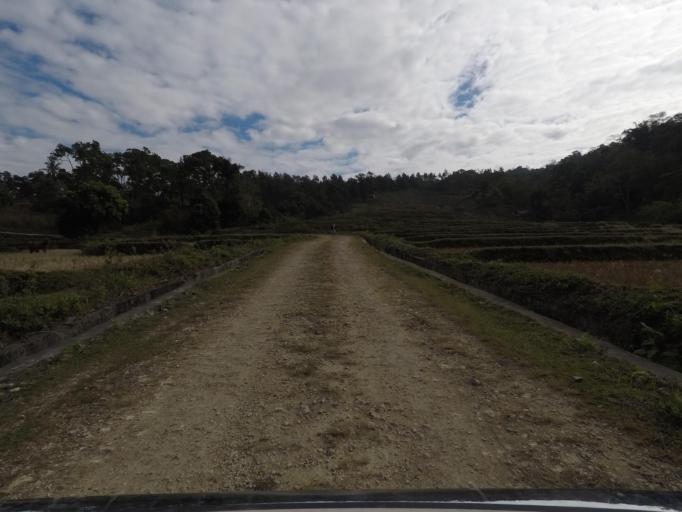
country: TL
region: Baucau
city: Venilale
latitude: -8.6537
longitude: 126.3945
